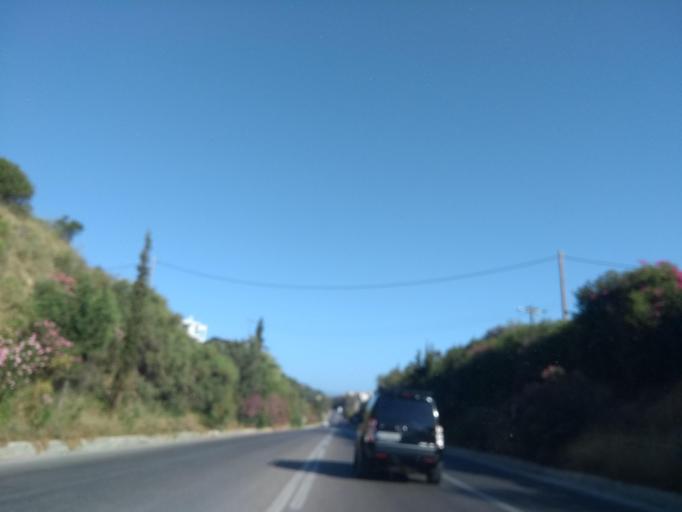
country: GR
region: Crete
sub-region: Nomos Chanias
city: Agia Marina
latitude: 35.5098
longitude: 23.9324
